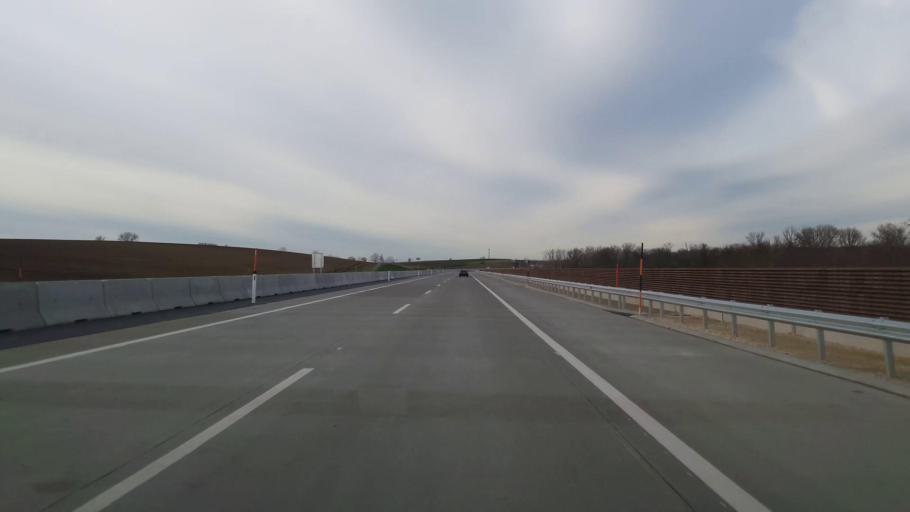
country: AT
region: Lower Austria
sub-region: Politischer Bezirk Mistelbach
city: Herrnbaumgarten
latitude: 48.6647
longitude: 16.6830
